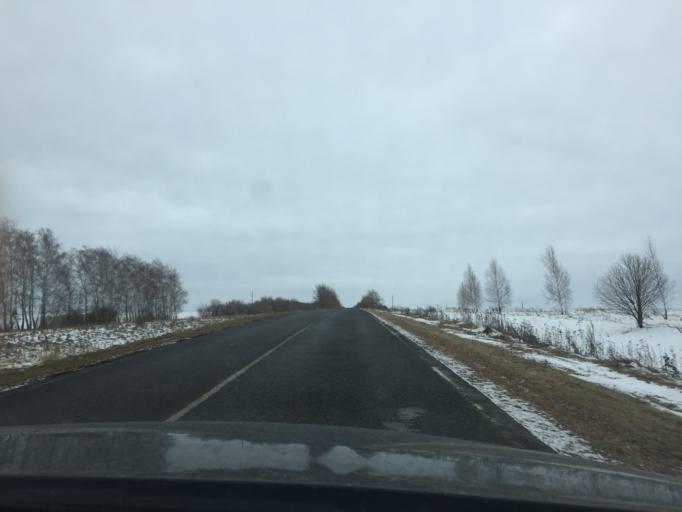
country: RU
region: Tula
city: Shchekino
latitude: 53.8265
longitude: 37.5167
